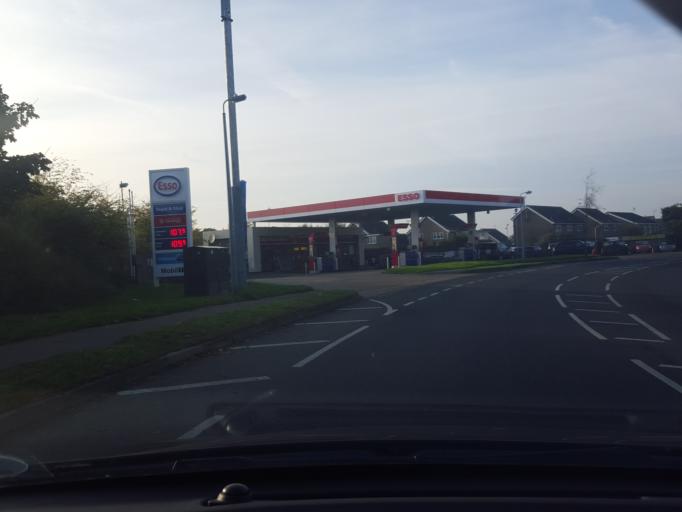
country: GB
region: England
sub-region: Essex
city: Frinton-on-Sea
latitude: 51.8382
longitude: 1.2404
